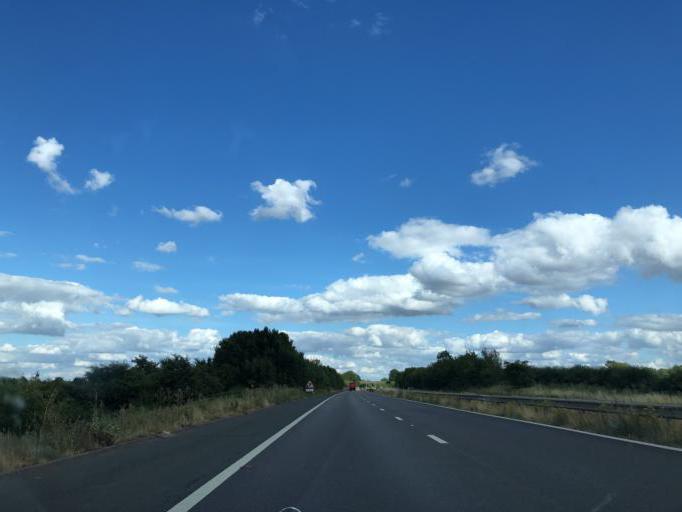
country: GB
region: England
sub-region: Warwickshire
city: Rugby
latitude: 52.3380
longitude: -1.2154
